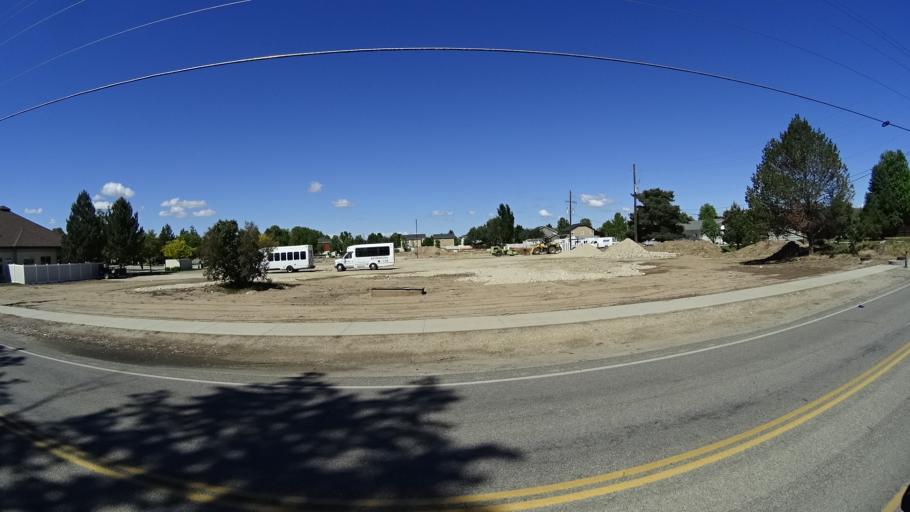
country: US
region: Idaho
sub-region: Ada County
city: Meridian
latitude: 43.6444
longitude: -116.3745
